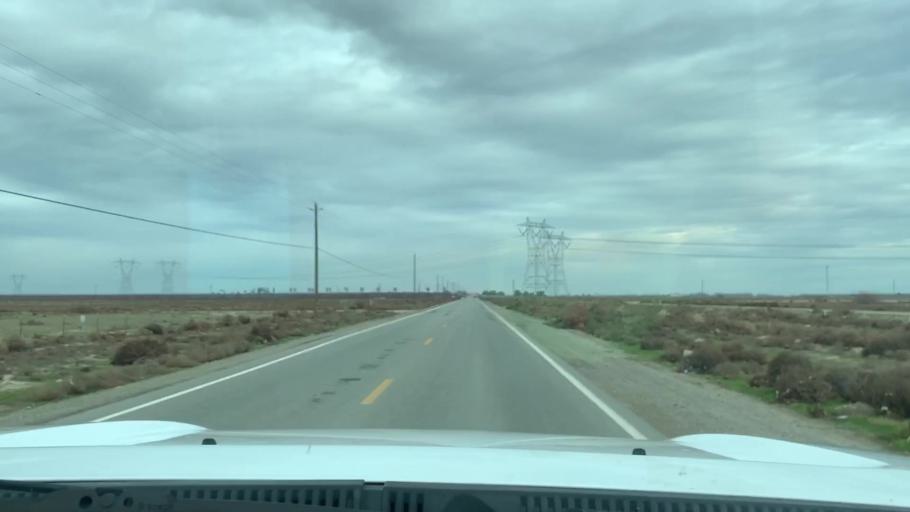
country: US
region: California
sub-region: Kern County
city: Rosedale
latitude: 35.2766
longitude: -119.2525
